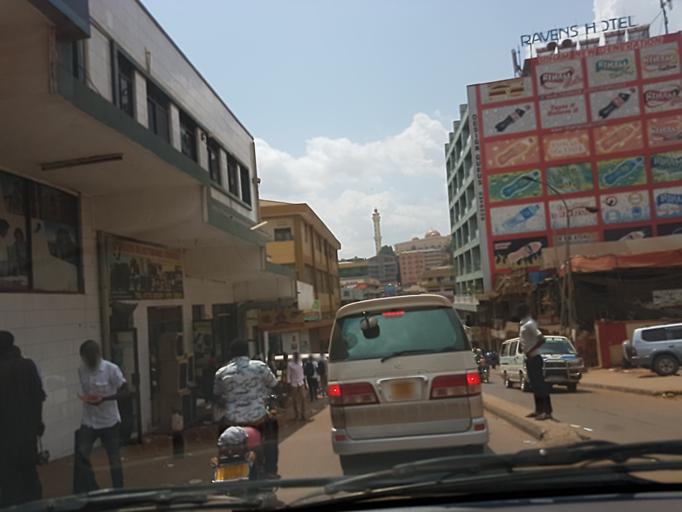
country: UG
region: Central Region
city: Kampala Central Division
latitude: 0.3175
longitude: 32.5733
